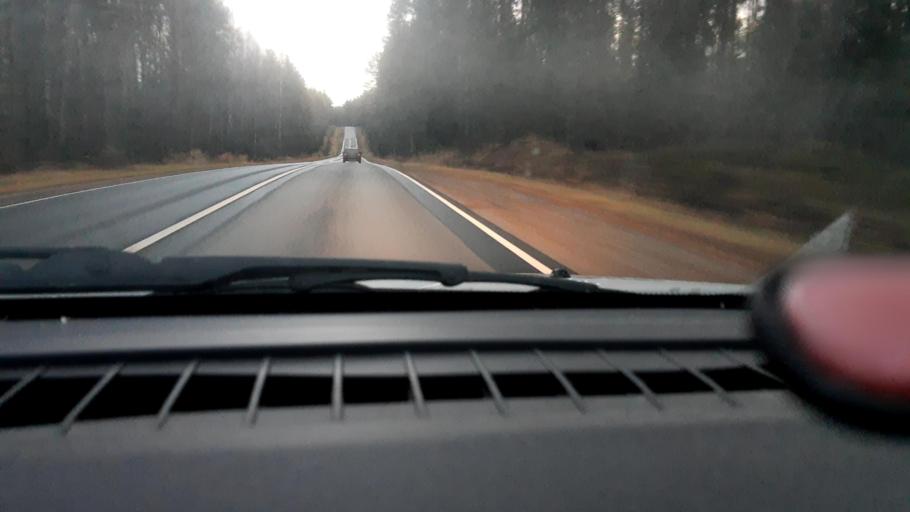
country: RU
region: Nizjnij Novgorod
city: Krasnyye Baki
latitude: 56.9986
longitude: 45.1133
